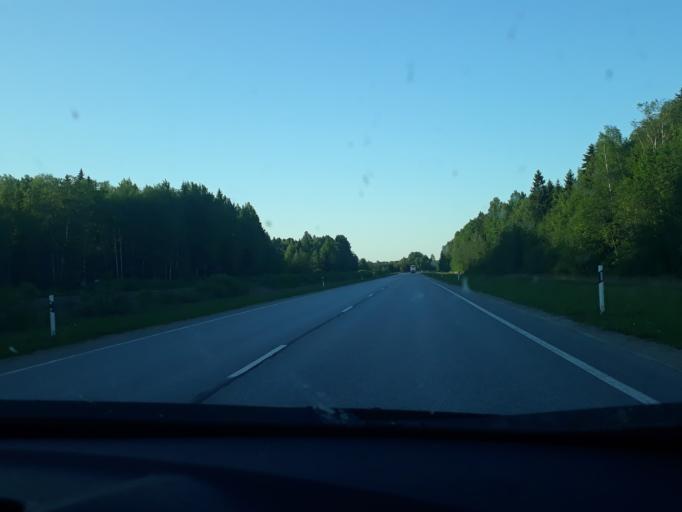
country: EE
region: Paernumaa
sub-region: Sindi linn
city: Sindi
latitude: 58.4558
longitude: 24.6959
